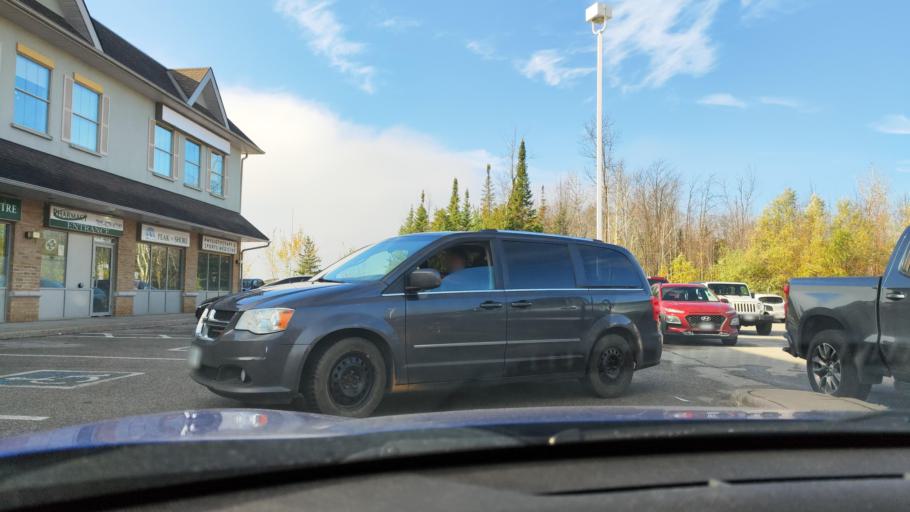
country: CA
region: Ontario
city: Wasaga Beach
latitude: 44.4687
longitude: -80.0759
